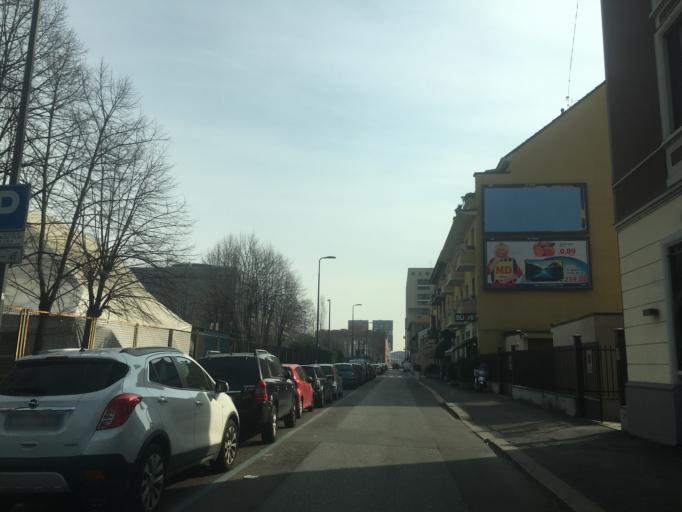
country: IT
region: Lombardy
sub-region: Citta metropolitana di Milano
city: Bresso
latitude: 45.5184
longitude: 9.2078
